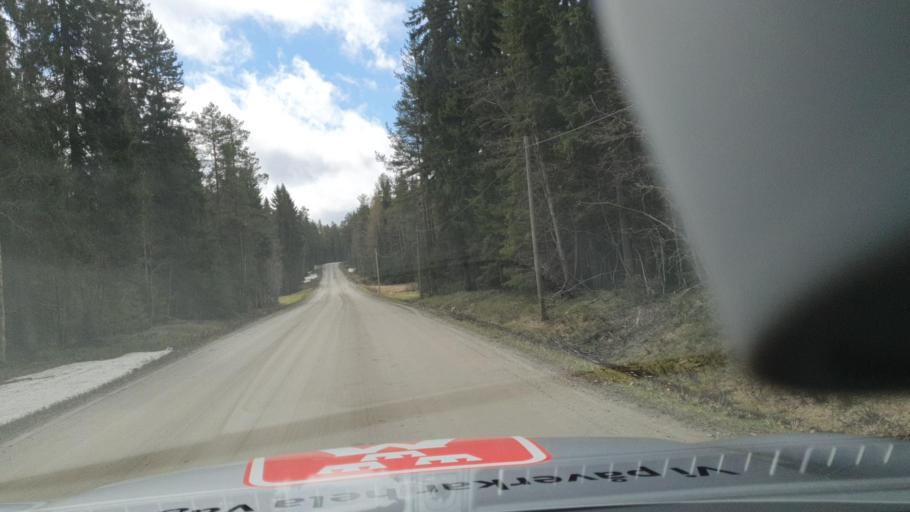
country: SE
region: Vaesterbotten
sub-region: Bjurholms Kommun
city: Bjurholm
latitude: 63.7009
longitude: 18.8985
